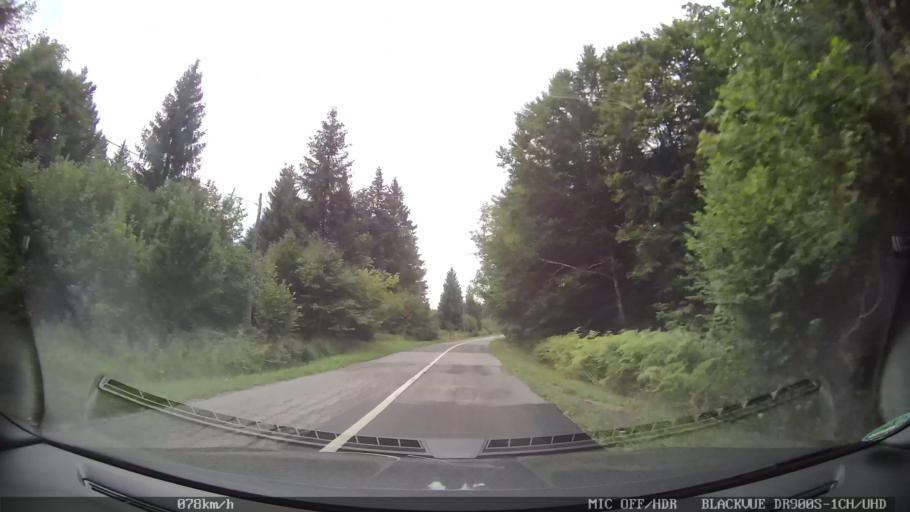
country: HR
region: Licko-Senjska
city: Jezerce
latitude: 44.9526
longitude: 15.5302
